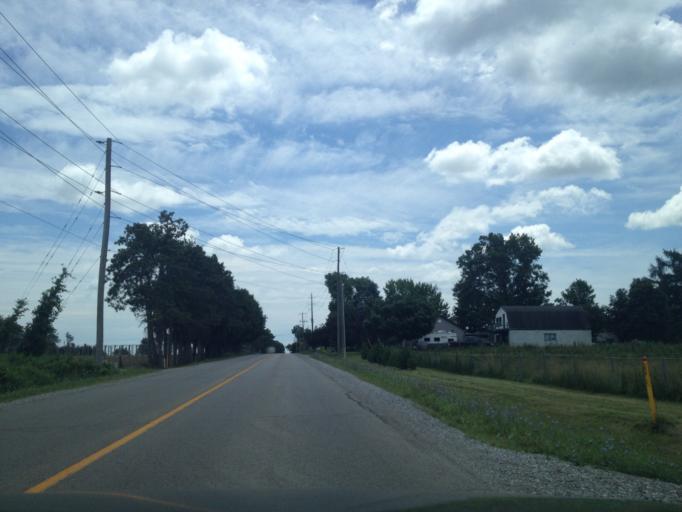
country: CA
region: Ontario
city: Norfolk County
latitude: 42.8234
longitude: -80.3309
